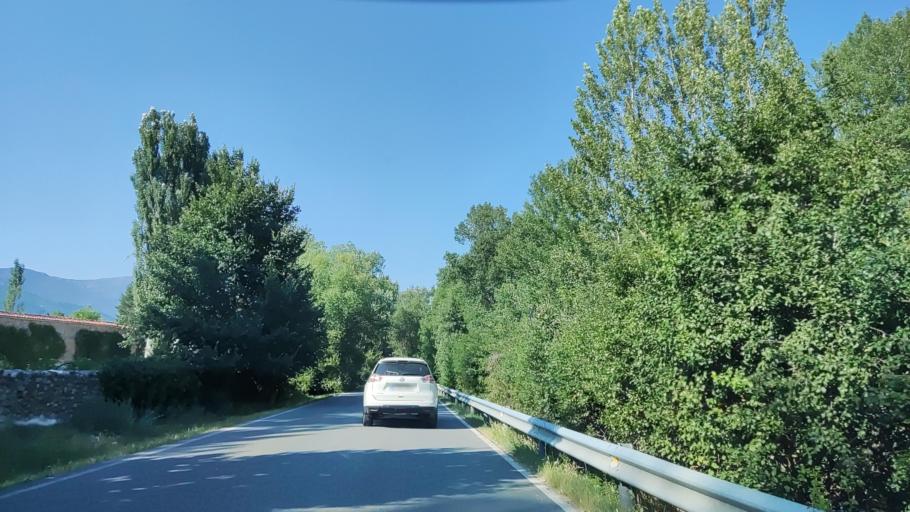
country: ES
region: Madrid
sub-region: Provincia de Madrid
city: Rascafria
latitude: 40.8884
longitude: -3.8862
